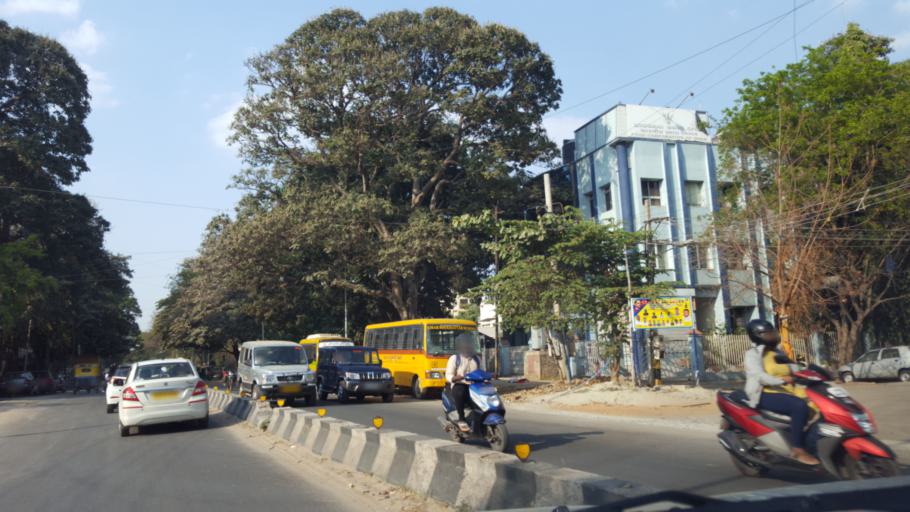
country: IN
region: Karnataka
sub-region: Bangalore Urban
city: Bangalore
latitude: 12.9243
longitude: 77.5970
